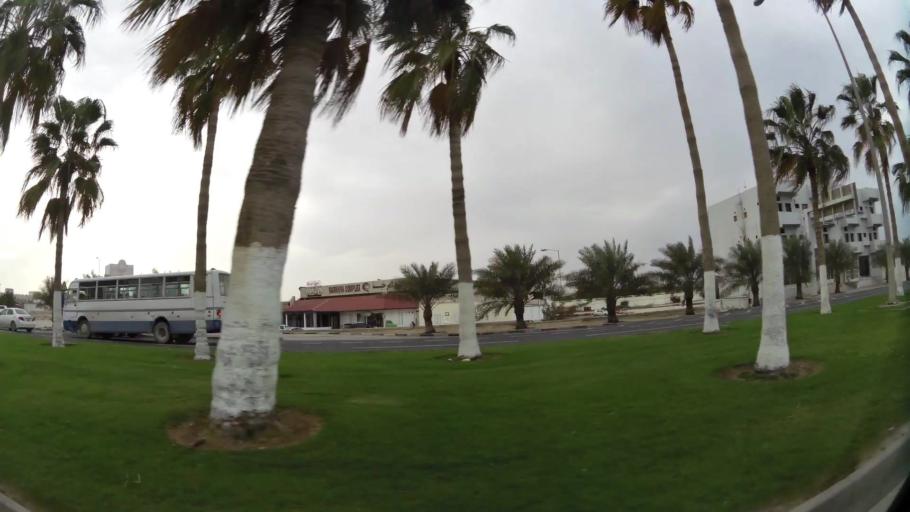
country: QA
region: Baladiyat ad Dawhah
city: Doha
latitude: 25.3193
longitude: 51.4967
